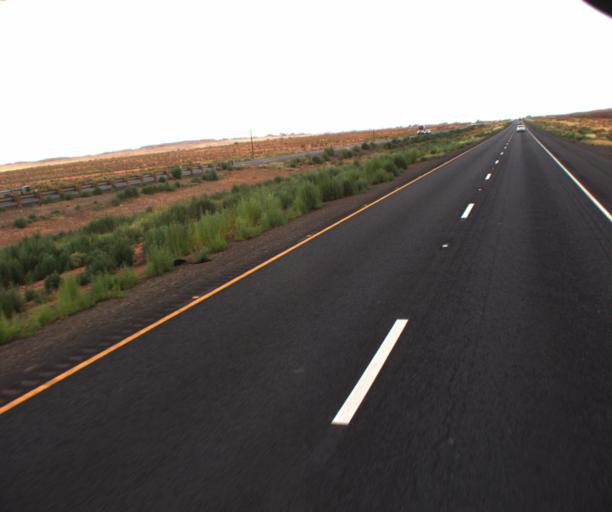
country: US
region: Arizona
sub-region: Coconino County
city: LeChee
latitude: 35.0496
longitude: -110.7751
